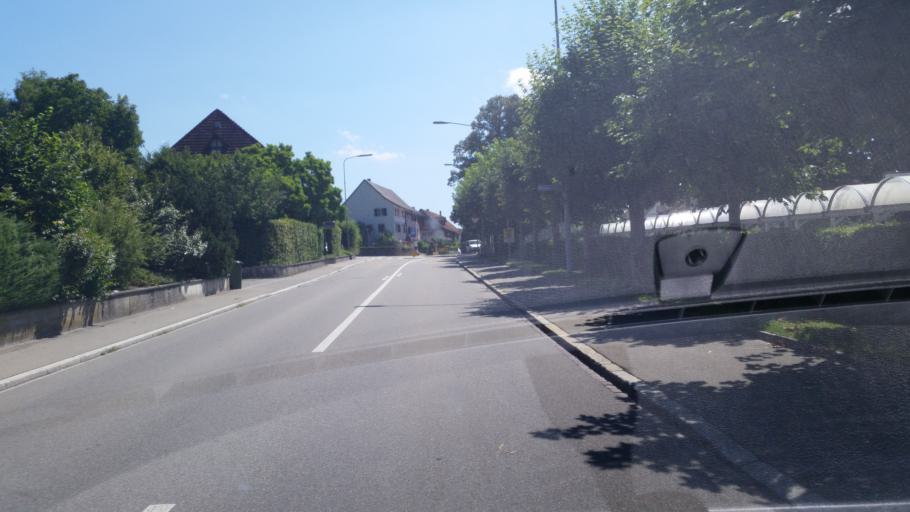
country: CH
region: Zurich
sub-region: Bezirk Buelach
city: Glattfelden
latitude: 47.5592
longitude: 8.5016
